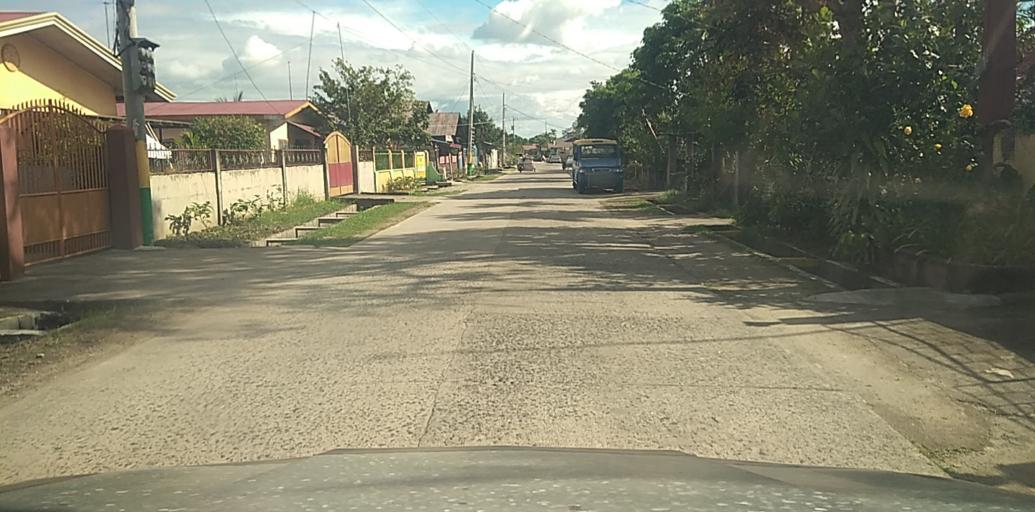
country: PH
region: Central Luzon
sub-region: Province of Pampanga
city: Panlinlang
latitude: 15.1880
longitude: 120.6925
